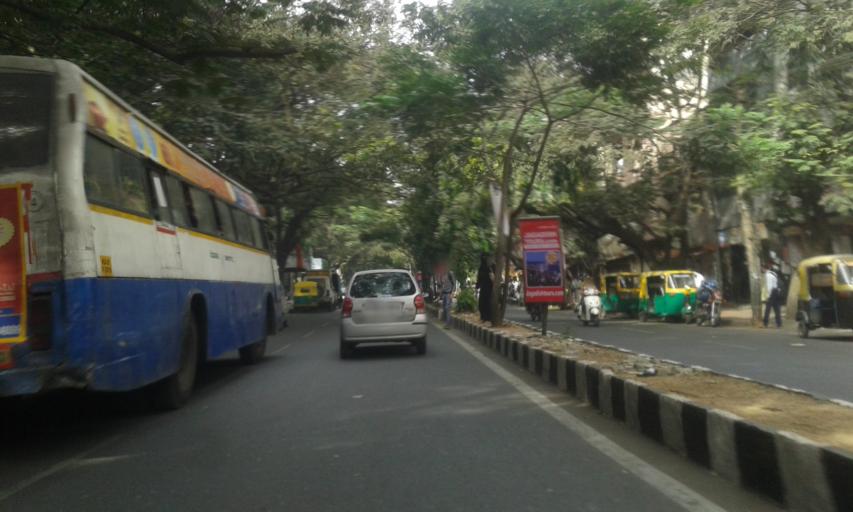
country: IN
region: Karnataka
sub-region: Bangalore Urban
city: Bangalore
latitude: 12.9270
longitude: 77.5931
